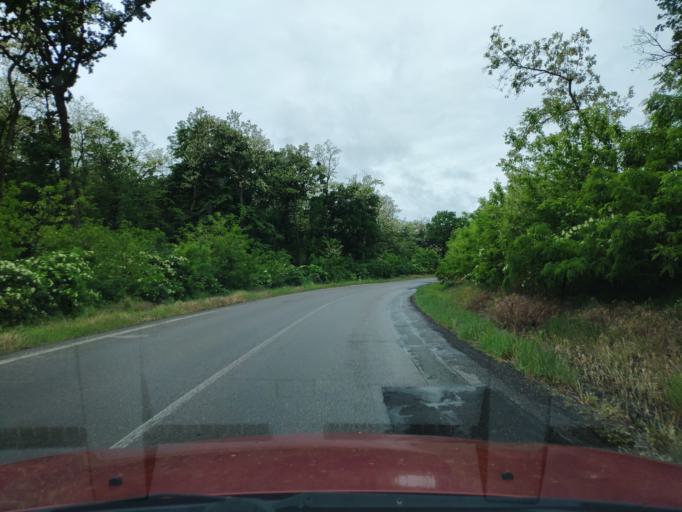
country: HU
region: Borsod-Abauj-Zemplen
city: Ricse
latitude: 48.4372
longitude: 21.9372
